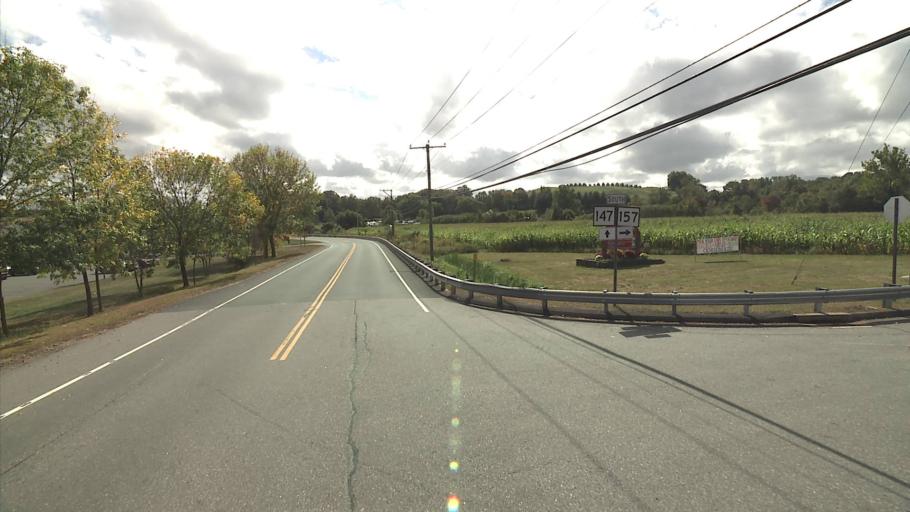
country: US
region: Connecticut
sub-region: Middlesex County
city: Durham
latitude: 41.5000
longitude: -72.7157
